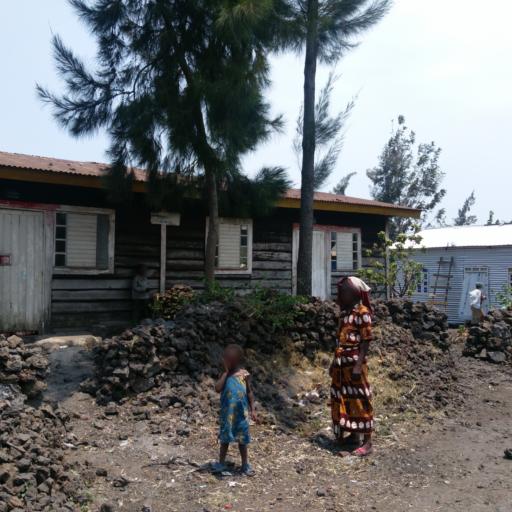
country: CD
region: Nord Kivu
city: Goma
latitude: -1.6435
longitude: 29.2290
